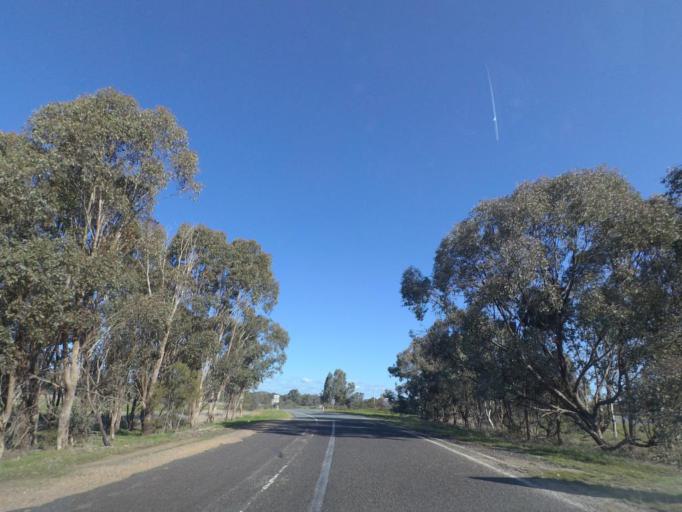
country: AU
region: Victoria
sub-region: Wangaratta
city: Wangaratta
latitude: -36.4226
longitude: 146.2637
